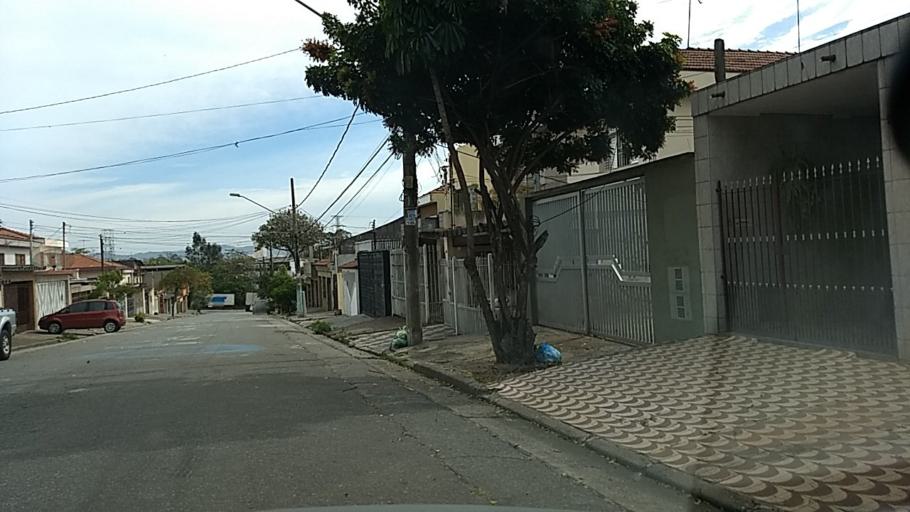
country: BR
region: Sao Paulo
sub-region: Guarulhos
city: Guarulhos
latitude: -23.5033
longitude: -46.5701
